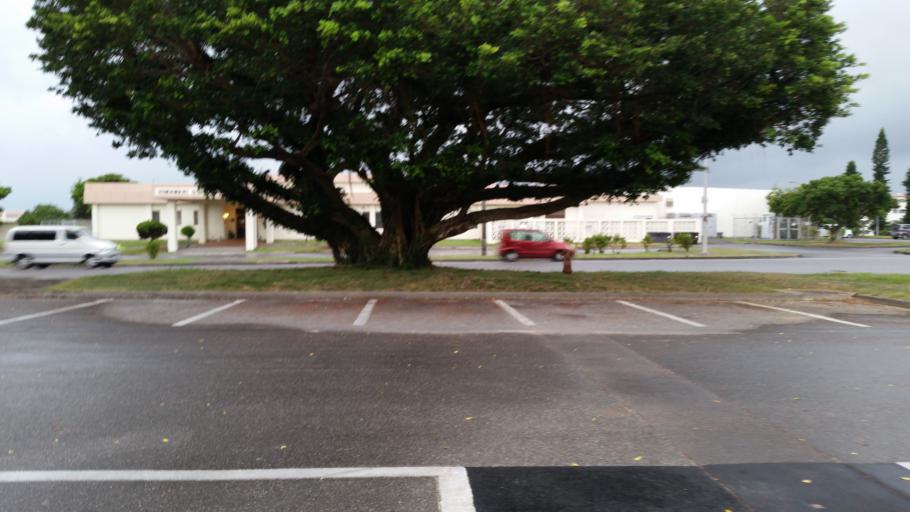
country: JP
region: Okinawa
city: Okinawa
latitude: 26.3418
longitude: 127.7837
